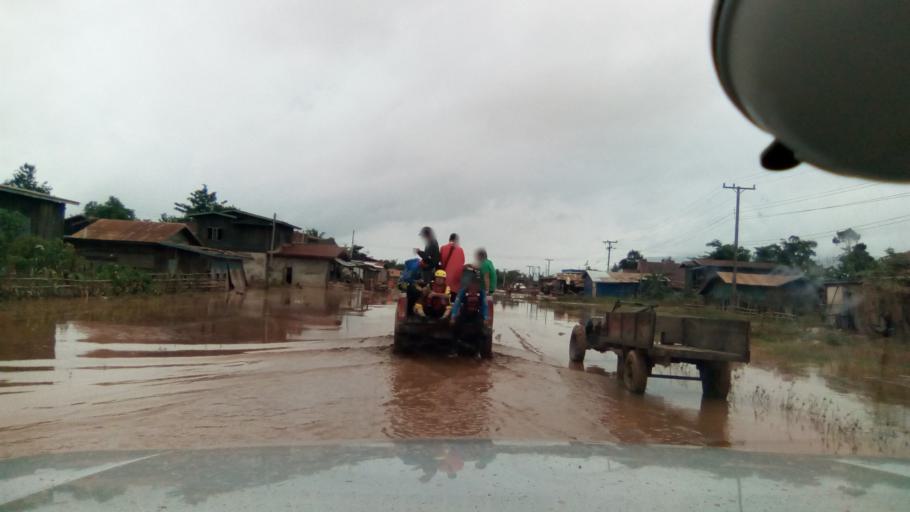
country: LA
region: Attapu
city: Attapu
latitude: 14.7006
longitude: 106.5302
